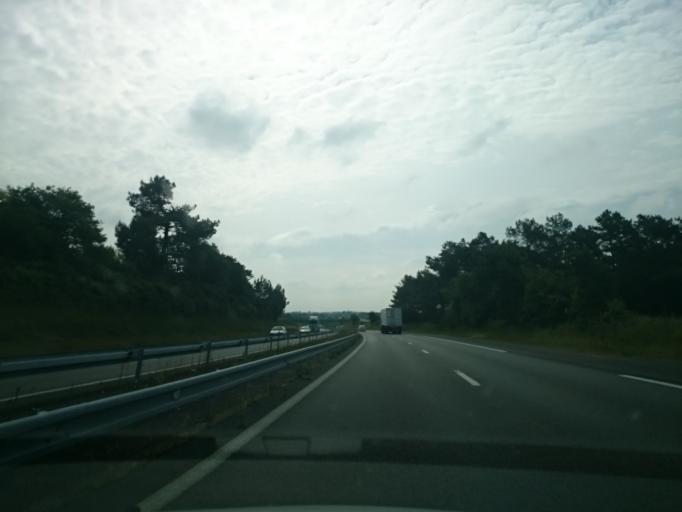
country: FR
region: Brittany
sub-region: Departement du Morbihan
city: Ambon
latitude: 47.5970
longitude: -2.5763
